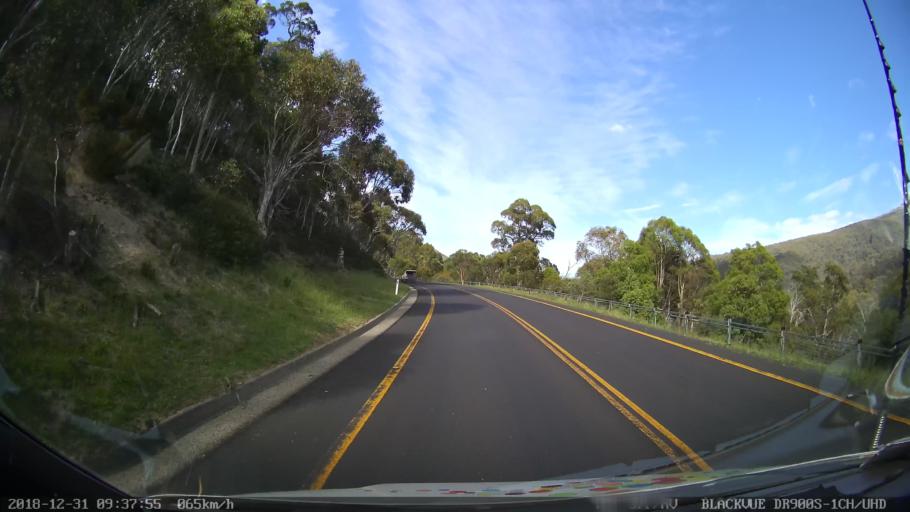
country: AU
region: New South Wales
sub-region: Snowy River
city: Jindabyne
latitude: -36.4706
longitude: 148.3721
